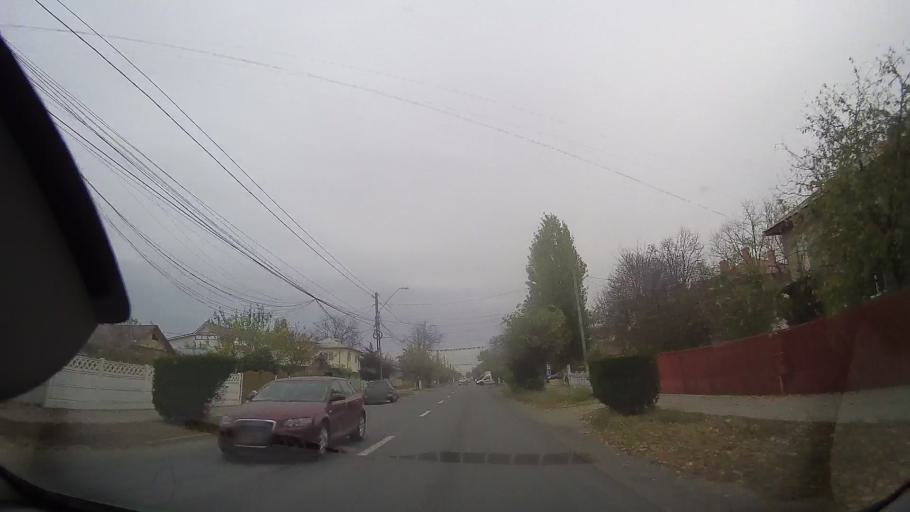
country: RO
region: Ialomita
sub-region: Oras Amara
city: Amara
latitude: 44.6160
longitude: 27.3143
